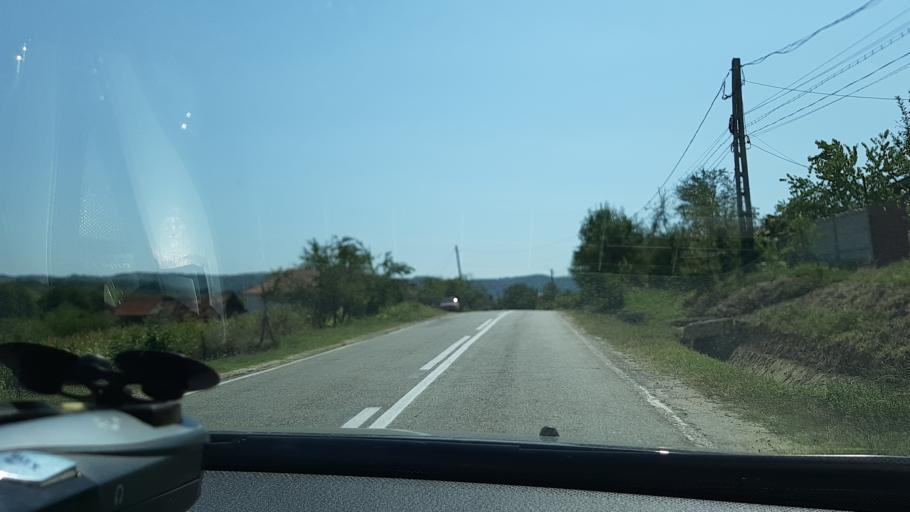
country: RO
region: Gorj
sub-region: Comuna Hurezani
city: Hurezani
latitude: 44.8251
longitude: 23.6460
